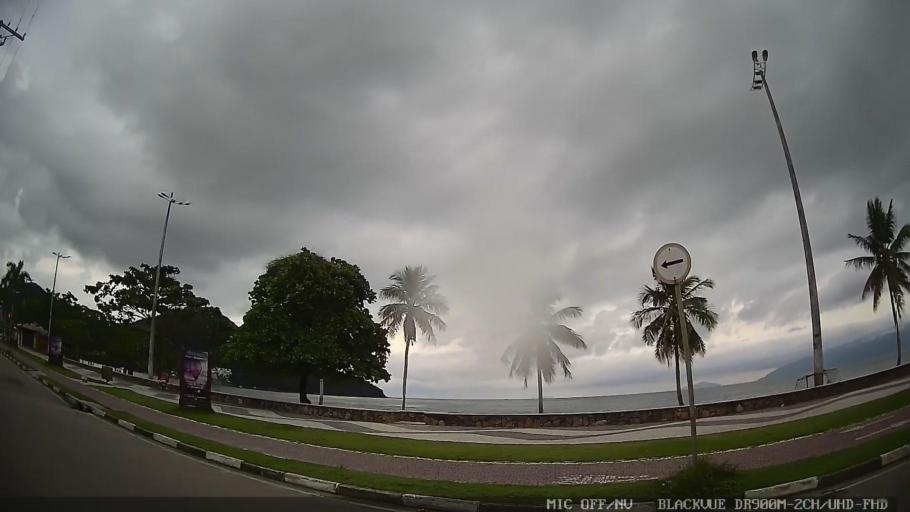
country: BR
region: Sao Paulo
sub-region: Caraguatatuba
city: Caraguatatuba
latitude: -23.6297
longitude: -45.3849
